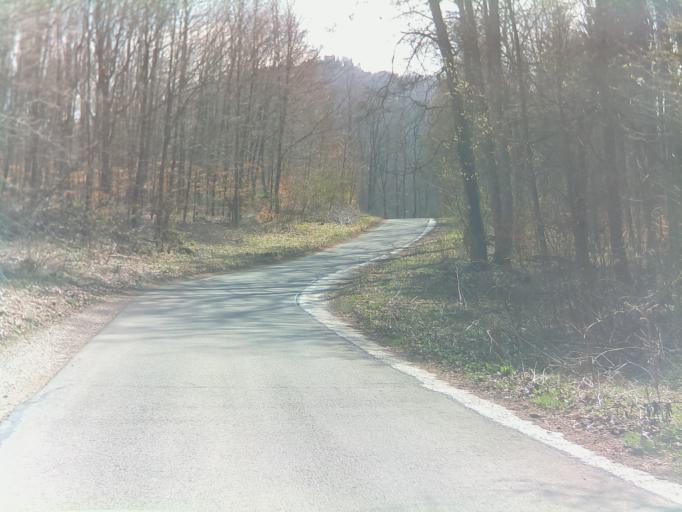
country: DE
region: Baden-Wuerttemberg
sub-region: Tuebingen Region
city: Bad Urach
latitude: 48.4448
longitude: 9.4148
